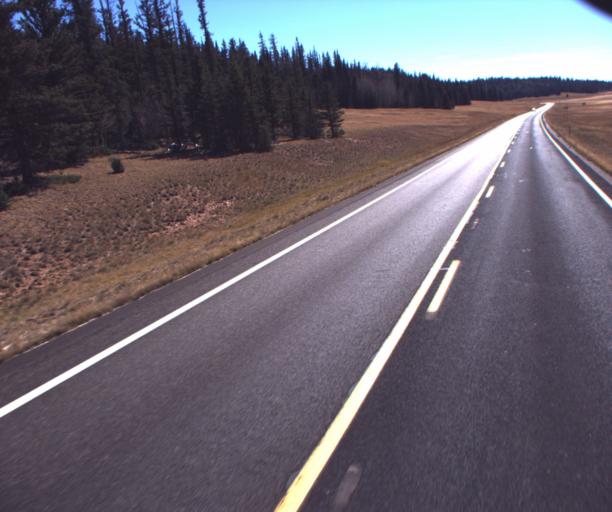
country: US
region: Arizona
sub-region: Coconino County
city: Grand Canyon
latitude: 36.4333
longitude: -112.1332
